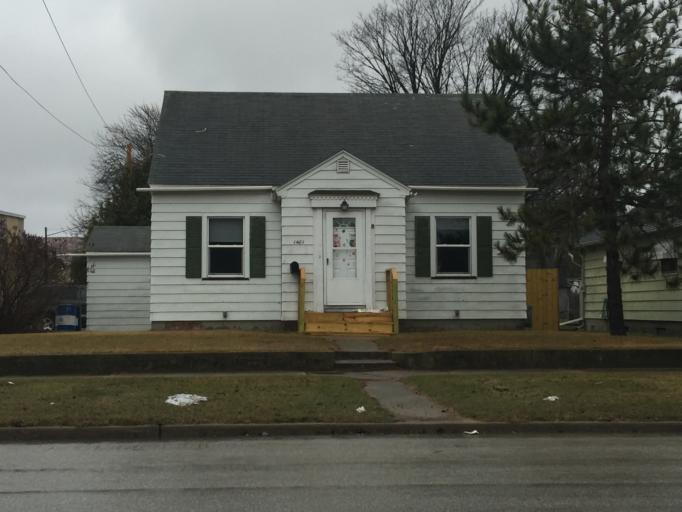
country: US
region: Michigan
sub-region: Menominee County
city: Menominee
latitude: 45.1171
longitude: -87.6201
